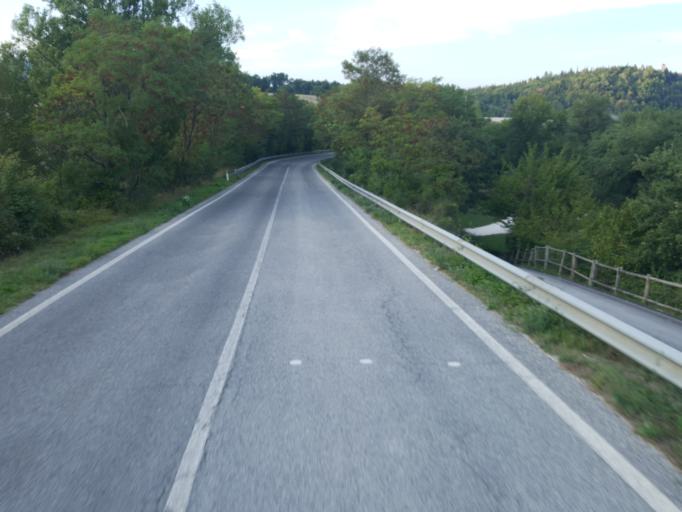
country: IT
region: The Marches
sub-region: Provincia di Ancona
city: Fabriano
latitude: 43.3315
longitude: 12.8312
